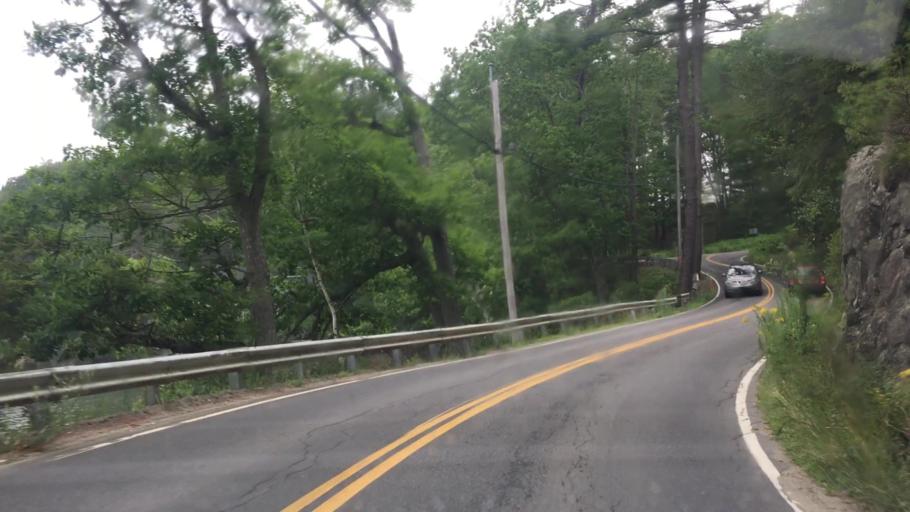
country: US
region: Maine
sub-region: Lincoln County
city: Wiscasset
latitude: 43.9951
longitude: -69.6498
